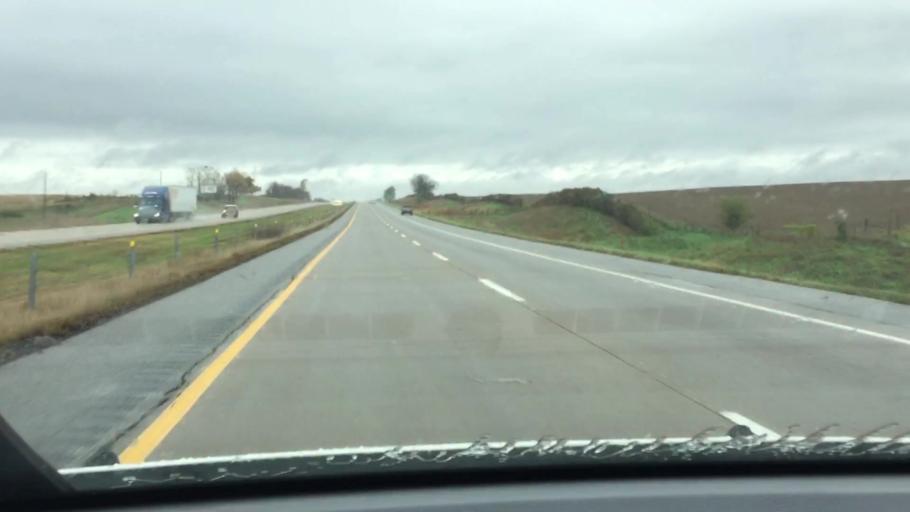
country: US
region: Iowa
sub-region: Poweshiek County
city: Brooklyn
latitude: 41.6963
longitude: -92.4058
